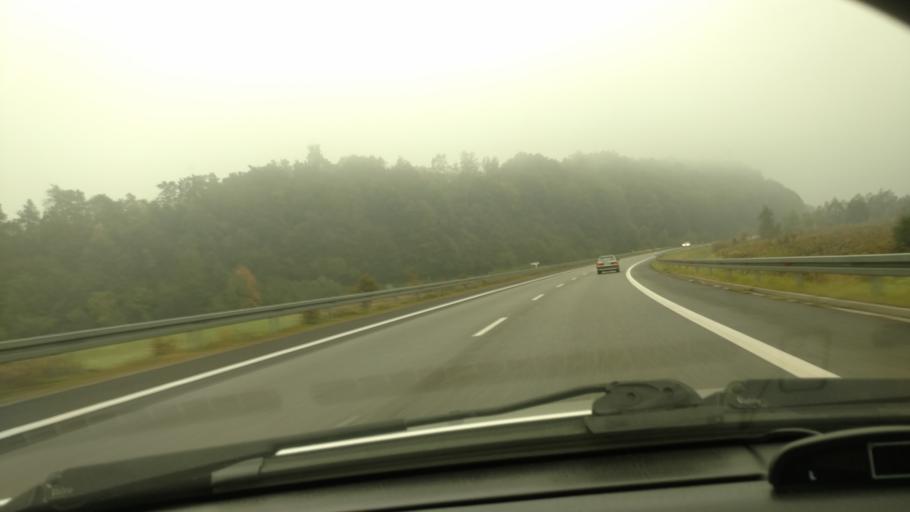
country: PL
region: Lesser Poland Voivodeship
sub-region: Powiat gorlicki
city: Biecz
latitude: 49.7324
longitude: 21.2720
